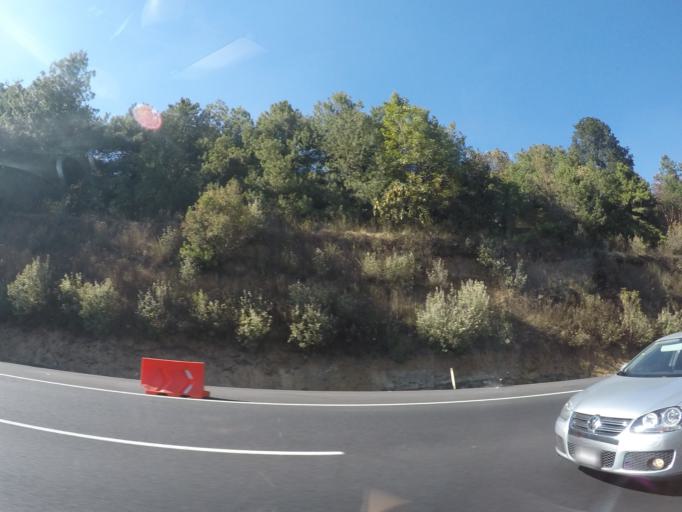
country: MX
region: Mexico City
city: Cuajimalpa
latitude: 19.3401
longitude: -99.2966
